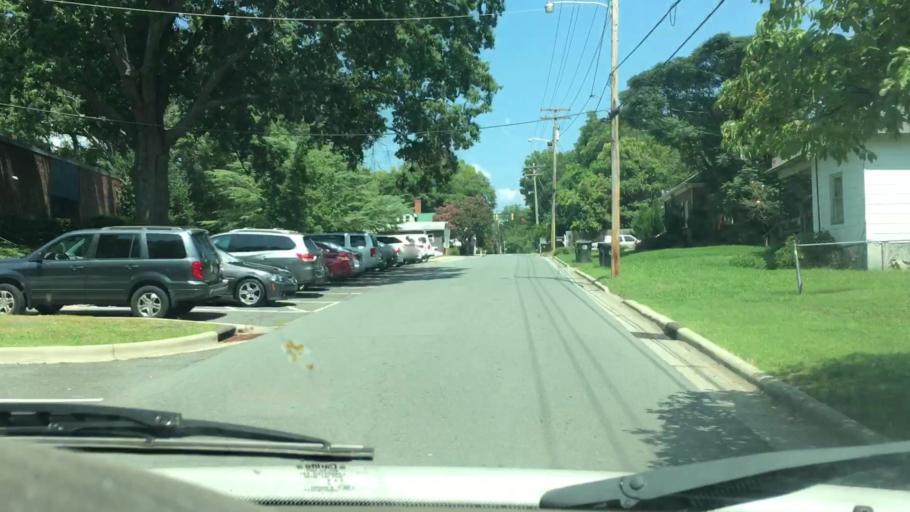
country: US
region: North Carolina
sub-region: Mecklenburg County
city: Cornelius
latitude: 35.4815
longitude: -80.8633
